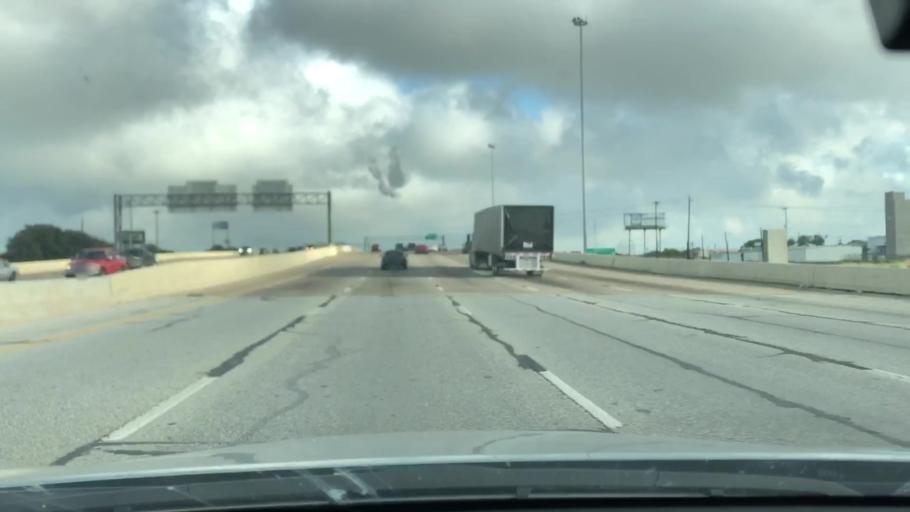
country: US
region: Texas
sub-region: Bexar County
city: Olmos Park
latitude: 29.4642
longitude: -98.5158
